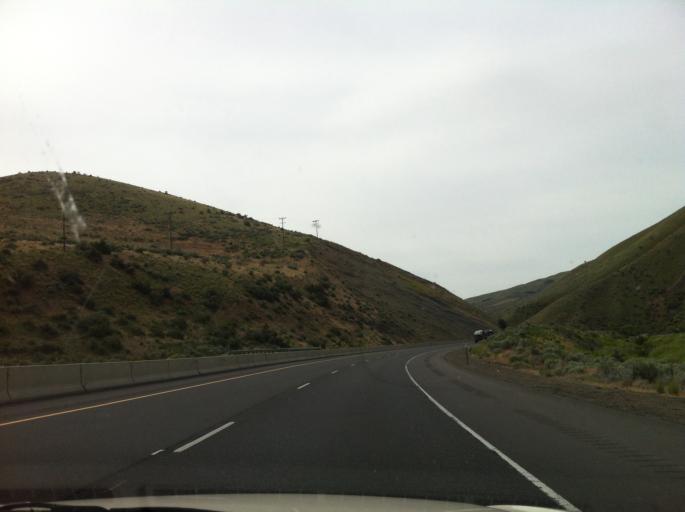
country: US
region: Idaho
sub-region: Washington County
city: Weiser
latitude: 44.4726
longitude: -117.3396
